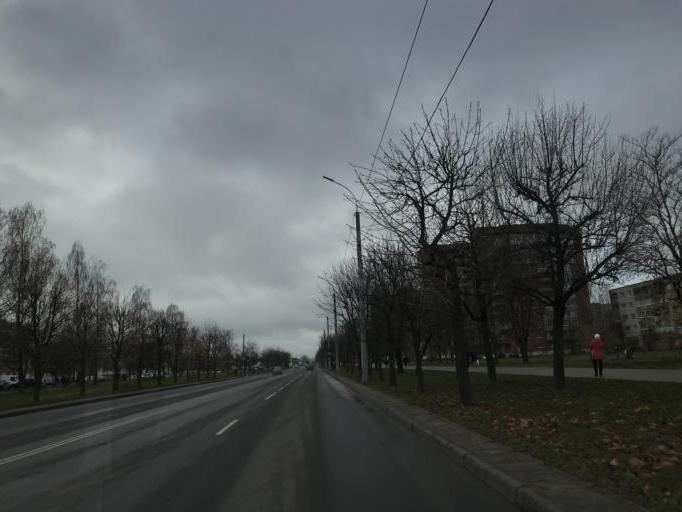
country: BY
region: Mogilev
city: Mahilyow
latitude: 53.8731
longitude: 30.3288
